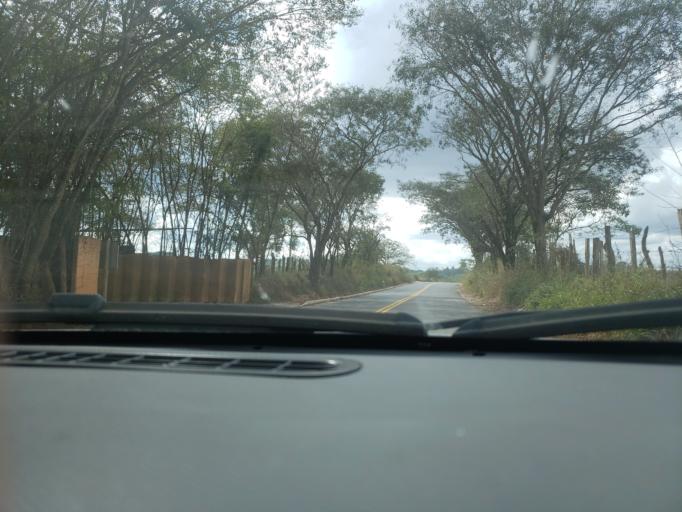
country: BR
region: Minas Gerais
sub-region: Campo Belo
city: Campo Belo
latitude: -20.9106
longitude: -45.2919
